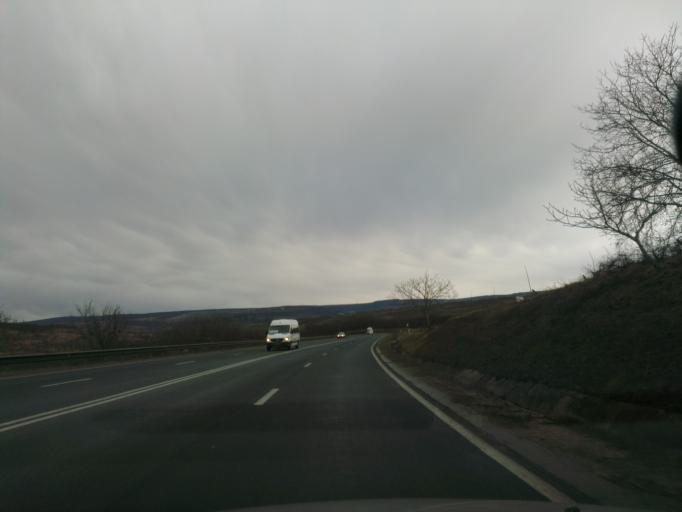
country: MD
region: Laloveni
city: Ialoveni
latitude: 46.9344
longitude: 28.7026
